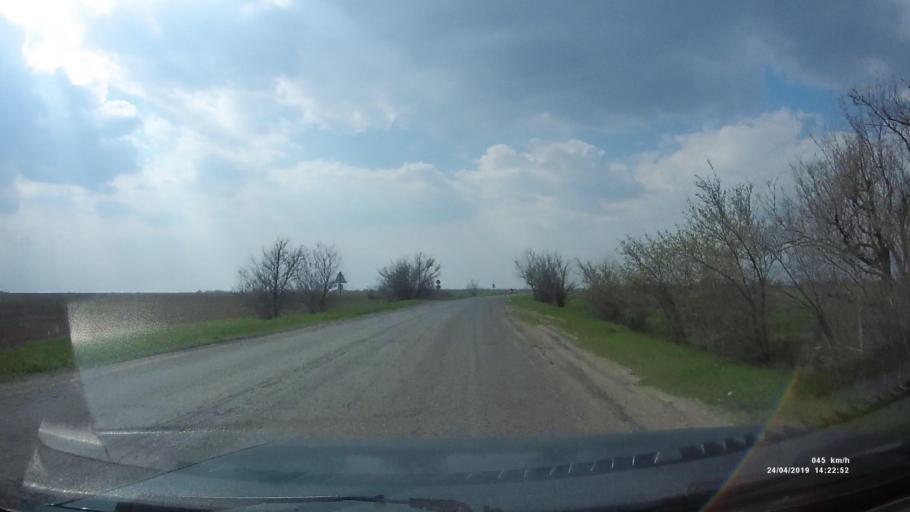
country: RU
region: Kalmykiya
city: Arshan'
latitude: 46.3181
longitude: 44.1210
